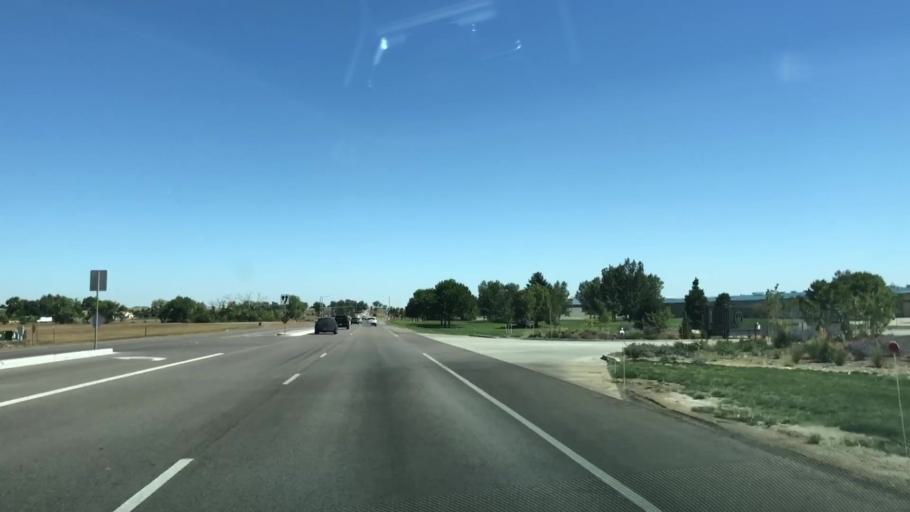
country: US
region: Colorado
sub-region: Weld County
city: Windsor
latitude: 40.5228
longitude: -104.9686
